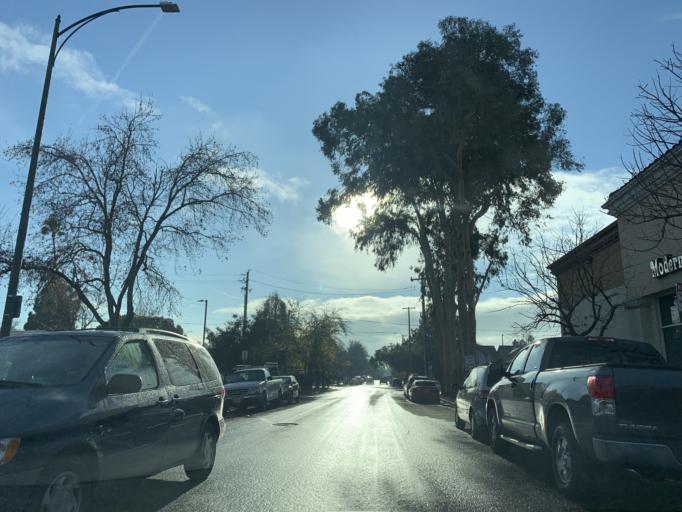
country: US
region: California
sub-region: Santa Clara County
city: San Jose
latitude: 37.3310
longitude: -121.8551
